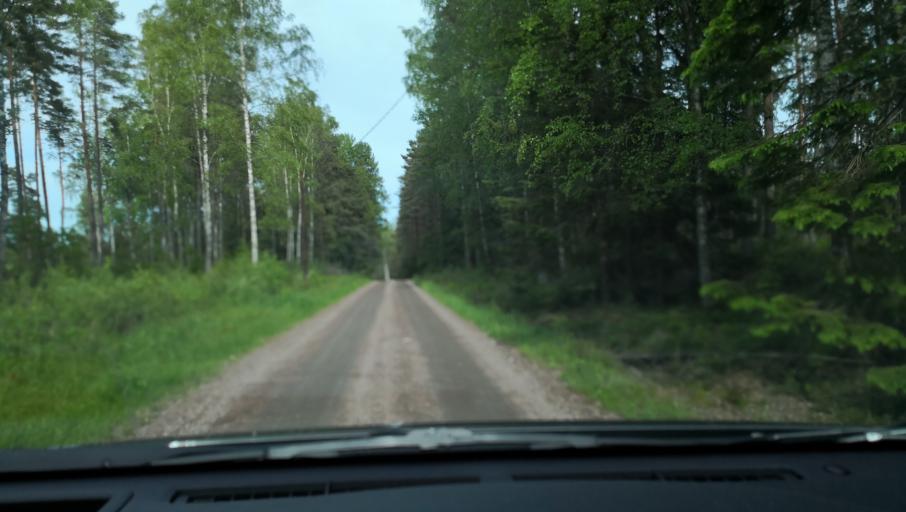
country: SE
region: Vaestmanland
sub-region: Arboga Kommun
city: Tyringe
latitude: 59.3636
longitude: 16.0118
